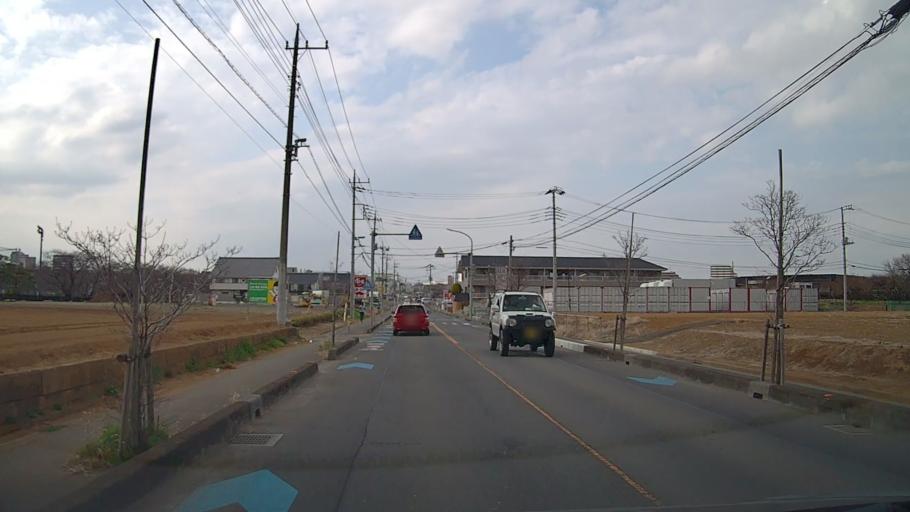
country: JP
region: Saitama
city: Asaka
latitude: 35.8145
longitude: 139.5965
